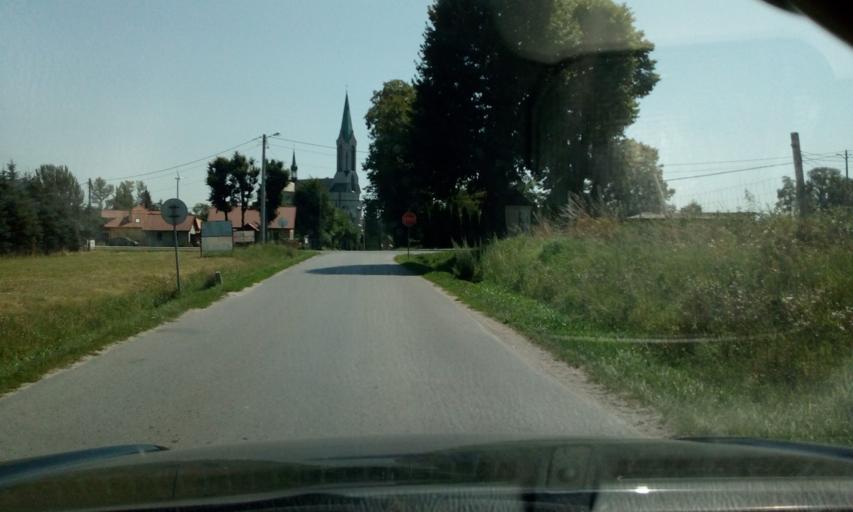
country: PL
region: Subcarpathian Voivodeship
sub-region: Powiat lancucki
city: Wysoka
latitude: 50.0459
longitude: 22.2472
